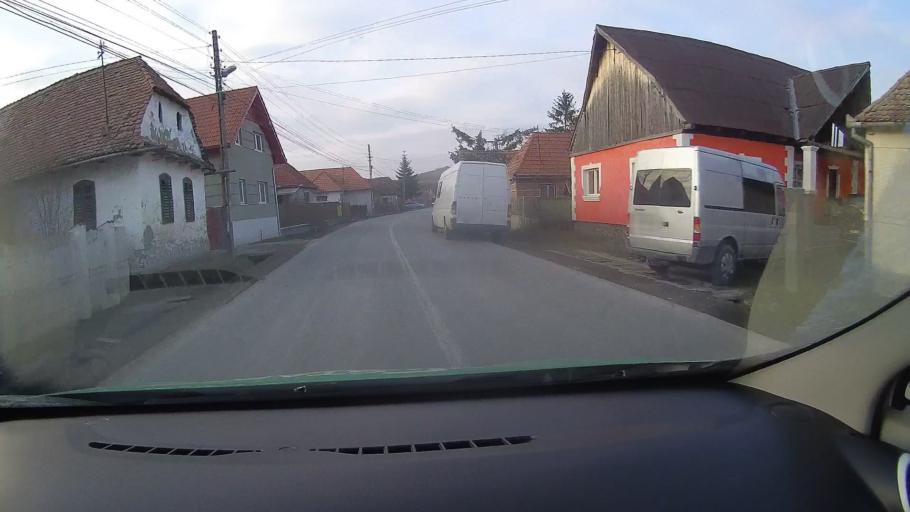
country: RO
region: Harghita
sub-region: Oras Cristuru Secuiesc
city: Cristuru Secuiesc
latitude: 46.3024
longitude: 25.0694
